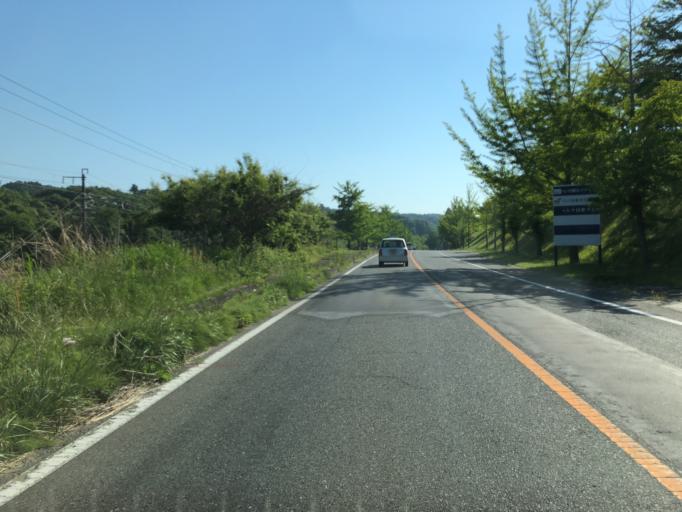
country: JP
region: Fukushima
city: Iwaki
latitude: 36.9426
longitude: 140.8192
